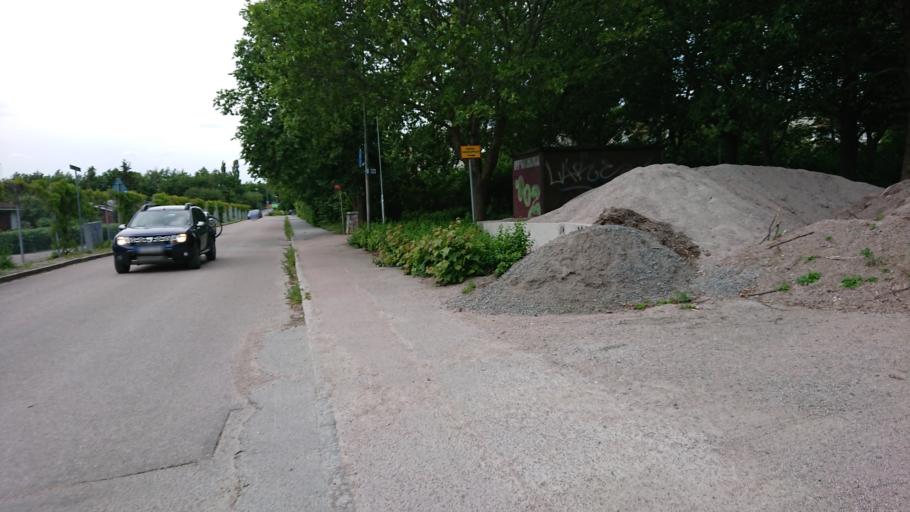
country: SE
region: Uppsala
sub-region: Uppsala Kommun
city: Gamla Uppsala
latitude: 59.8762
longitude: 17.6134
